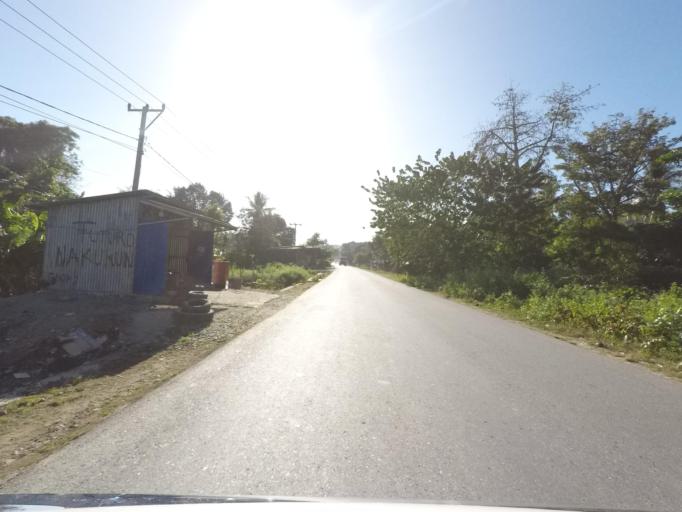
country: TL
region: Dili
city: Dili
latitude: -8.5552
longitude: 125.6553
